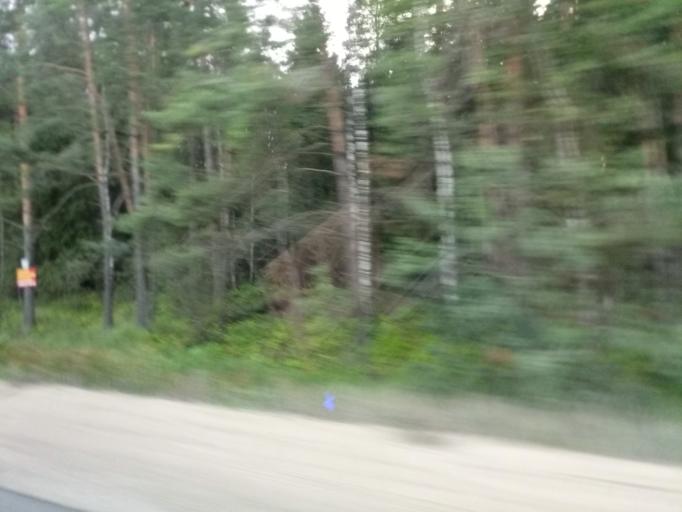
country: RU
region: Moskovskaya
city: Noginsk-9
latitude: 56.0893
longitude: 38.5793
